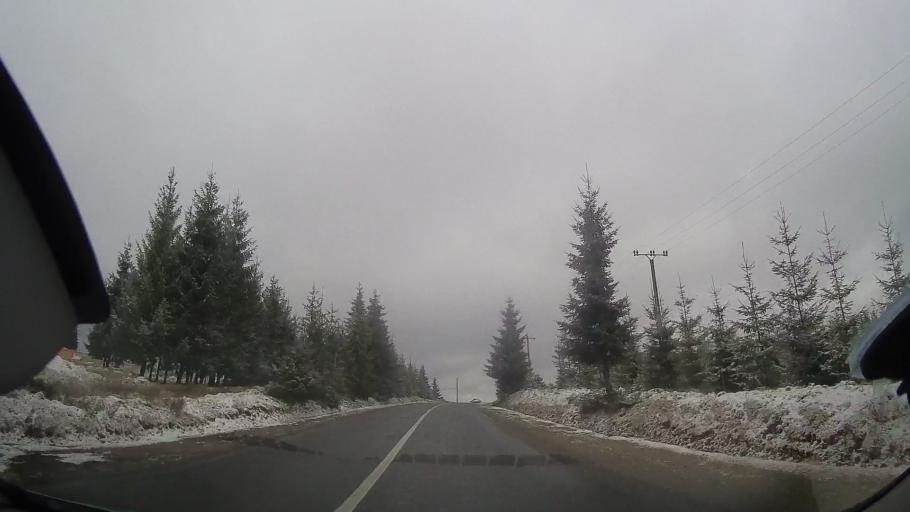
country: RO
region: Cluj
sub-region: Comuna Belis
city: Belis
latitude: 46.6937
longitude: 23.0392
